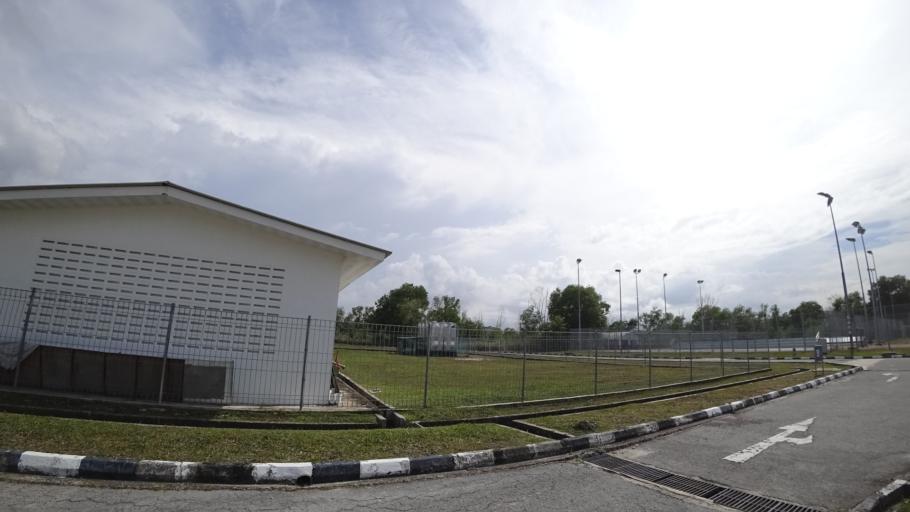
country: BN
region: Tutong
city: Tutong
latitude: 4.8127
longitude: 114.6588
